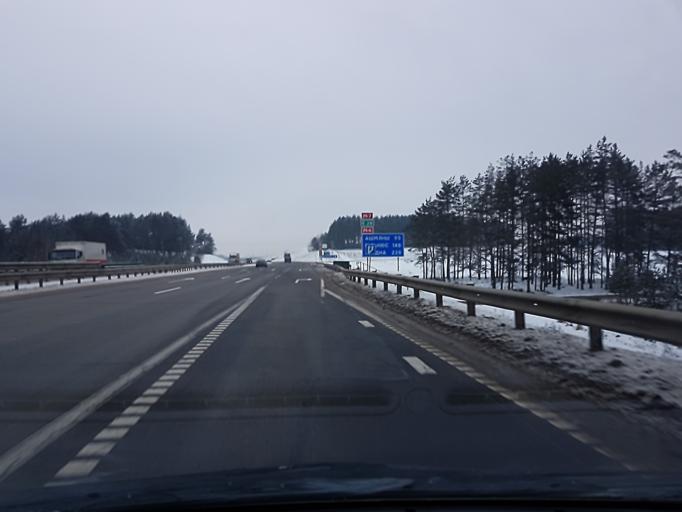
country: BY
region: Minsk
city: Rakaw
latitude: 53.9685
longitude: 27.0841
